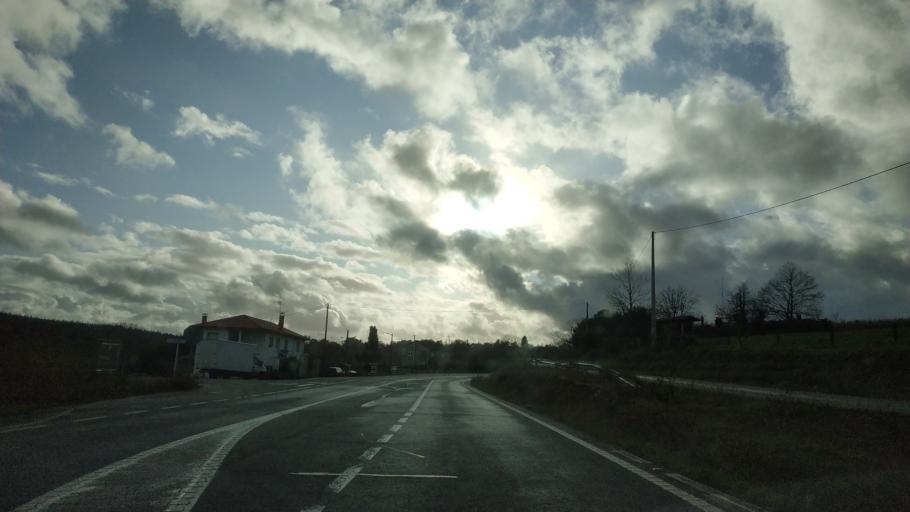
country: ES
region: Galicia
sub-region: Provincia da Coruna
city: Arzua
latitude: 42.8892
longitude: -8.1770
